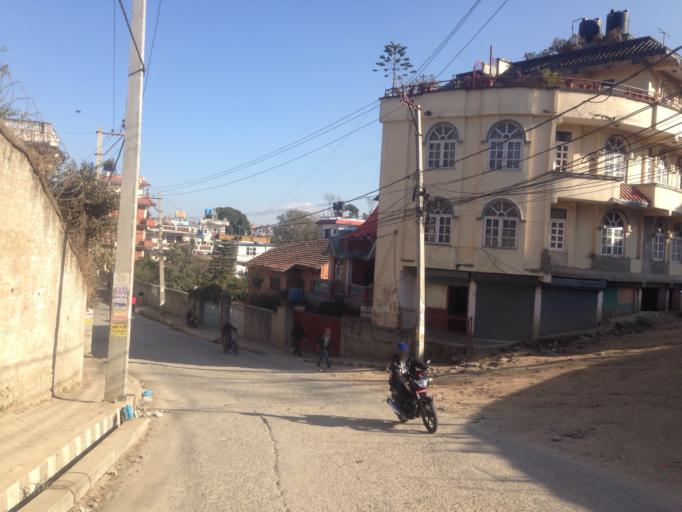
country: NP
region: Central Region
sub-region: Bagmati Zone
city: Kathmandu
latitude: 27.7216
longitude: 85.3360
